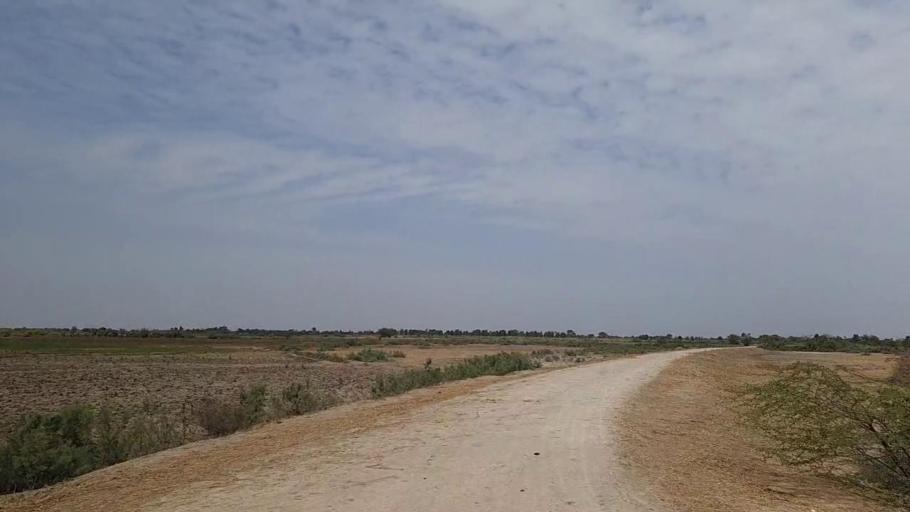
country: PK
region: Sindh
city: Daro Mehar
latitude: 24.7860
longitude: 68.2055
